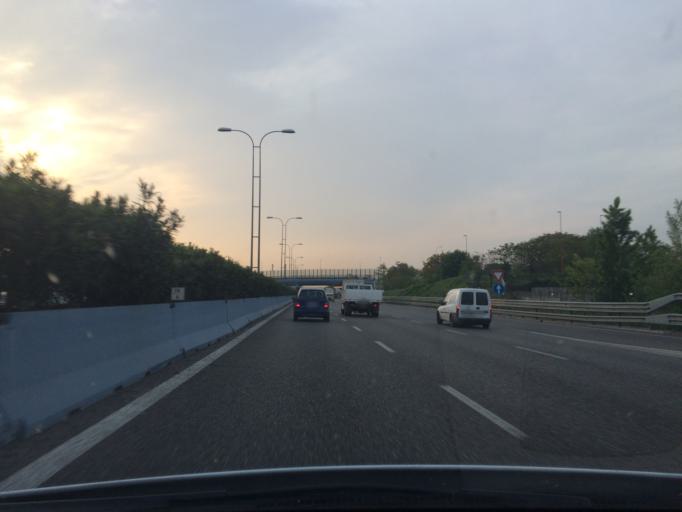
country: IT
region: Lombardy
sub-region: Provincia di Brescia
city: Brescia
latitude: 45.5213
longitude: 10.1890
